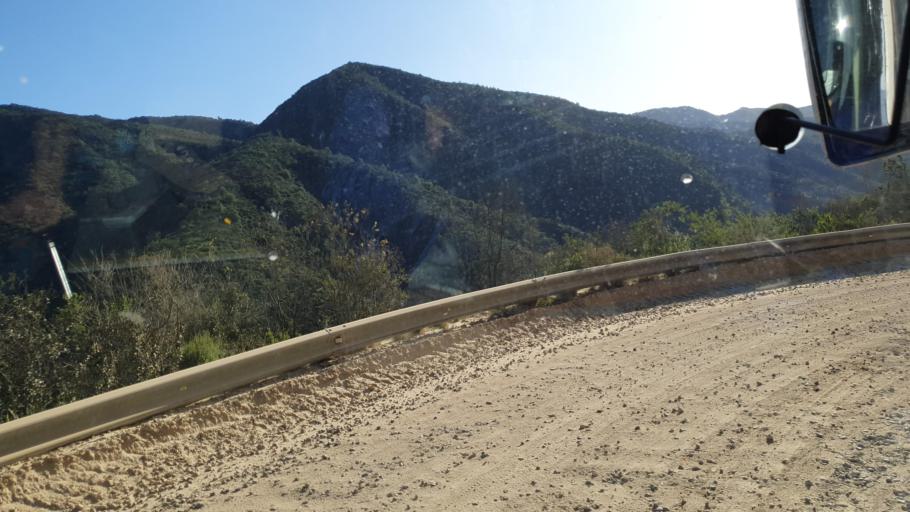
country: CL
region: Valparaiso
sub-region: Provincia de Marga Marga
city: Limache
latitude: -33.1988
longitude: -71.2656
